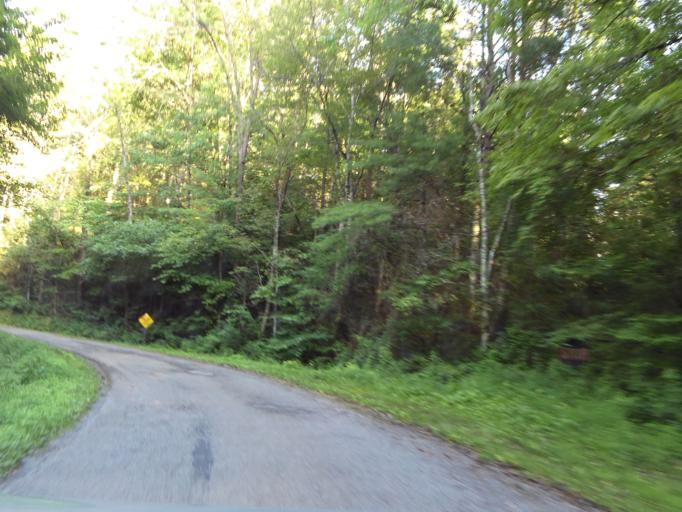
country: US
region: Tennessee
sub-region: Blount County
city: Maryville
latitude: 35.6076
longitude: -83.9426
